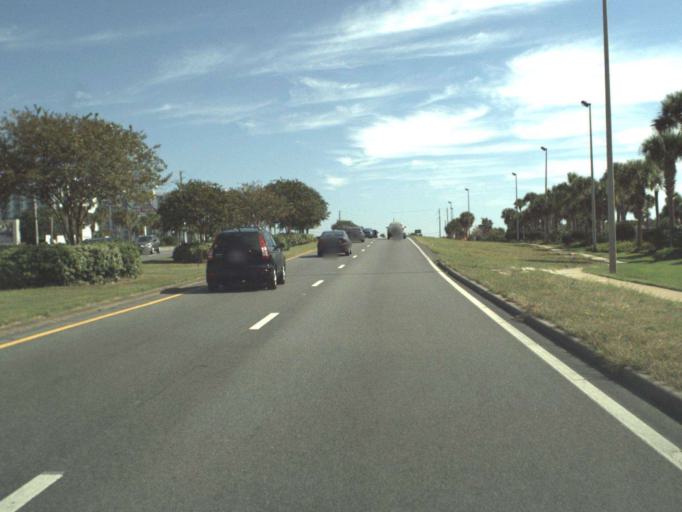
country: US
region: Florida
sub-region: Okaloosa County
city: Destin
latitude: 30.3858
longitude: -86.4599
